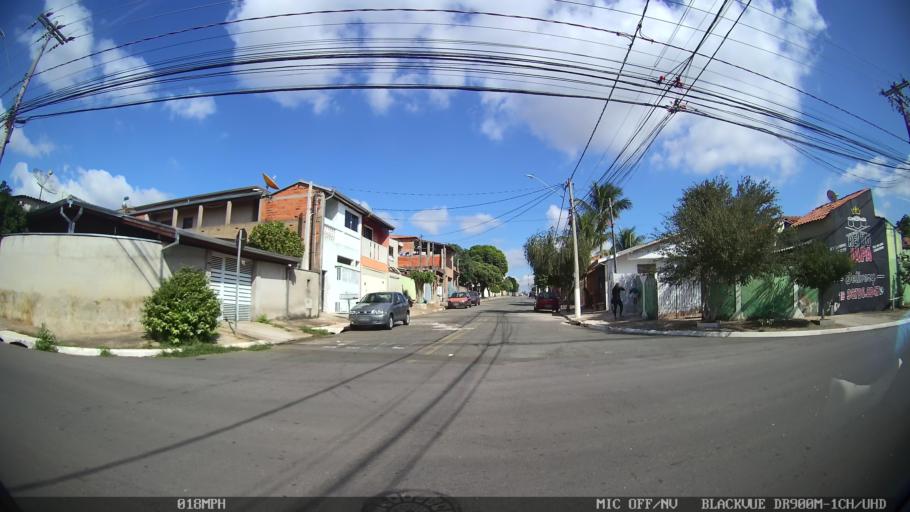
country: BR
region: Sao Paulo
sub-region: Hortolandia
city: Hortolandia
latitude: -22.8982
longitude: -47.1960
